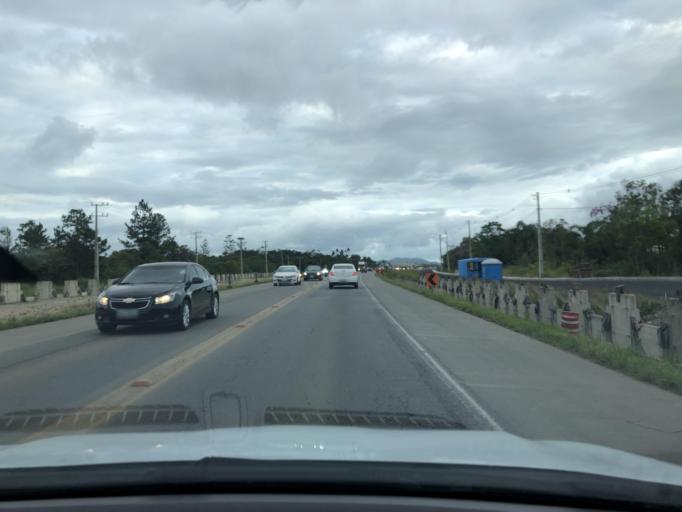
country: BR
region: Santa Catarina
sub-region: Joinville
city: Joinville
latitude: -26.3936
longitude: -48.7378
